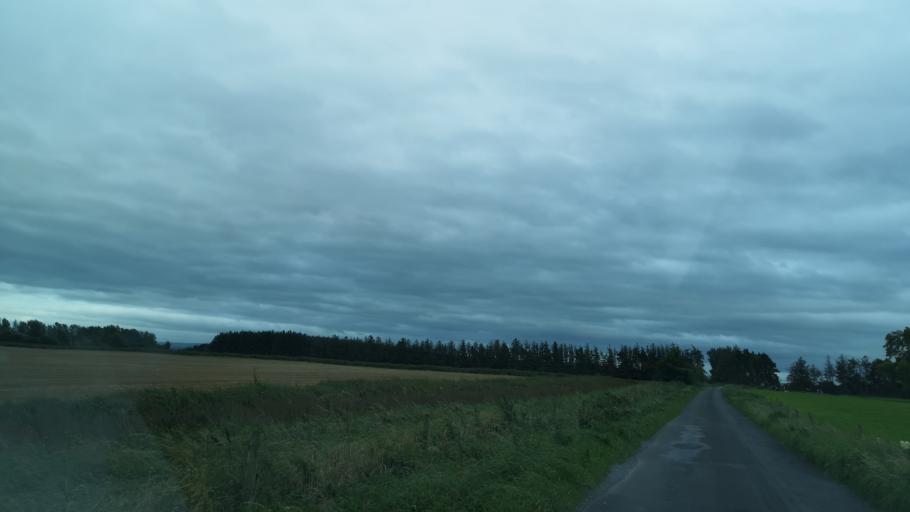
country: IE
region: Leinster
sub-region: Uibh Fhaili
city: Ferbane
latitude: 53.2110
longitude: -7.7241
